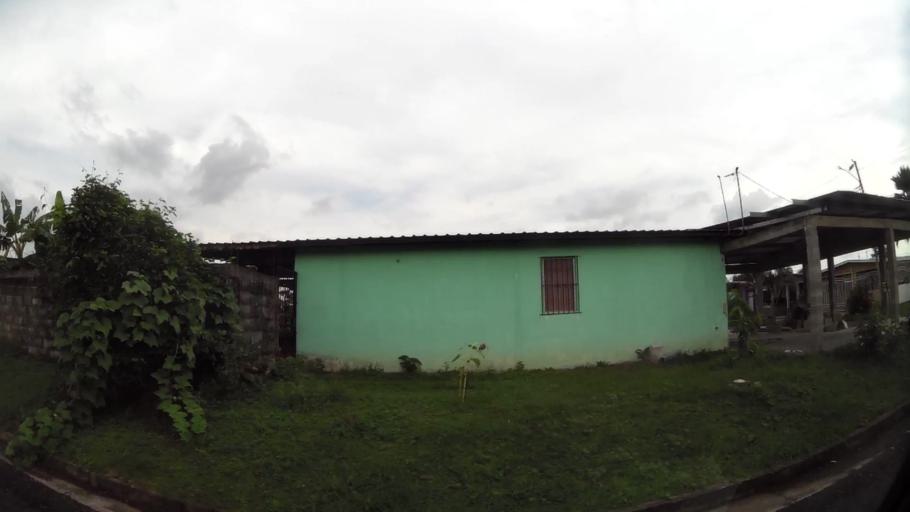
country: PA
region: Panama
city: Cabra Numero Uno
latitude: 9.0936
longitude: -79.3450
